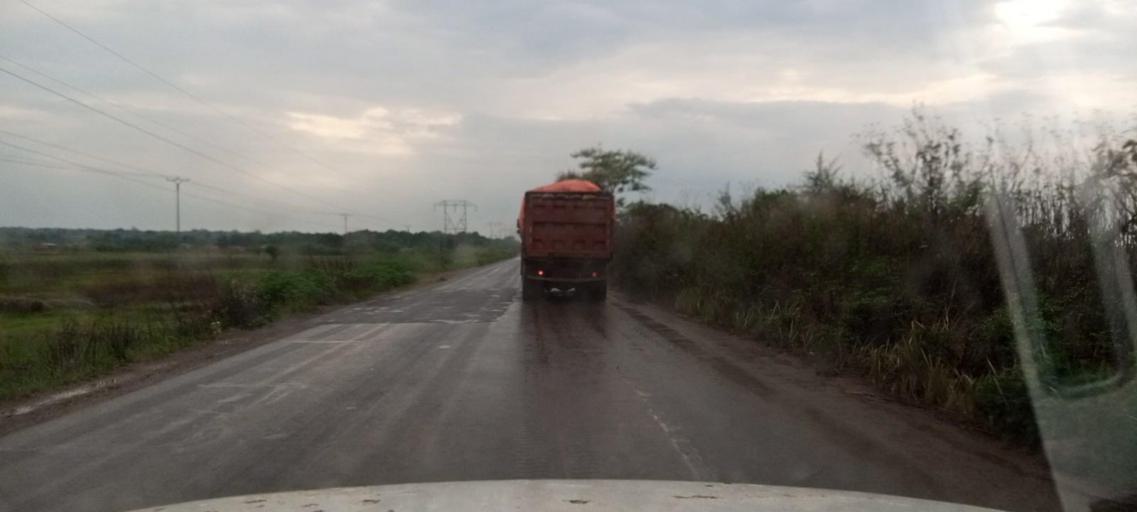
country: CD
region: Katanga
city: Likasi
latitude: -11.0025
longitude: 26.8535
